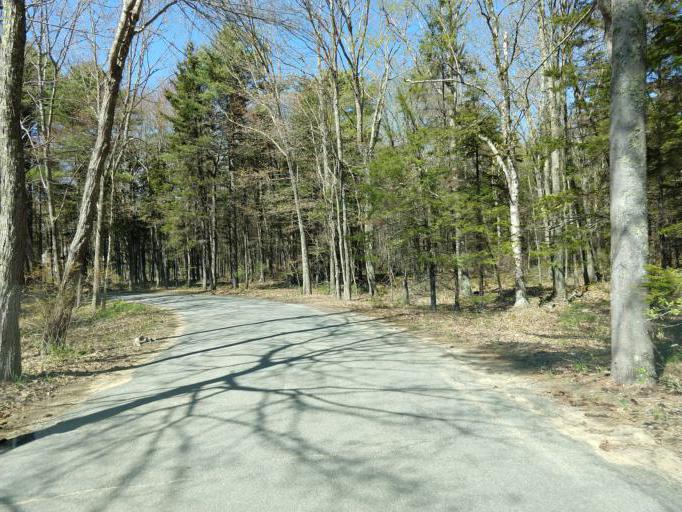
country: US
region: Maine
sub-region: York County
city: Wells Beach Station
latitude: 43.3408
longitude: -70.5534
